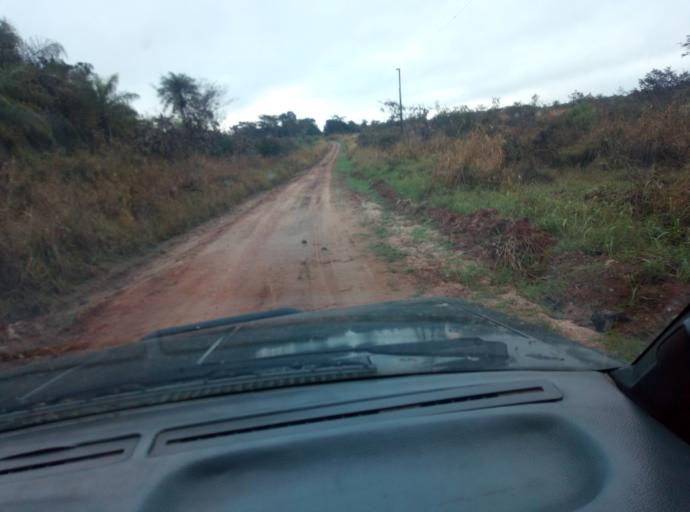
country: PY
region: Caaguazu
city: Carayao
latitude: -25.1904
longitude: -56.3501
